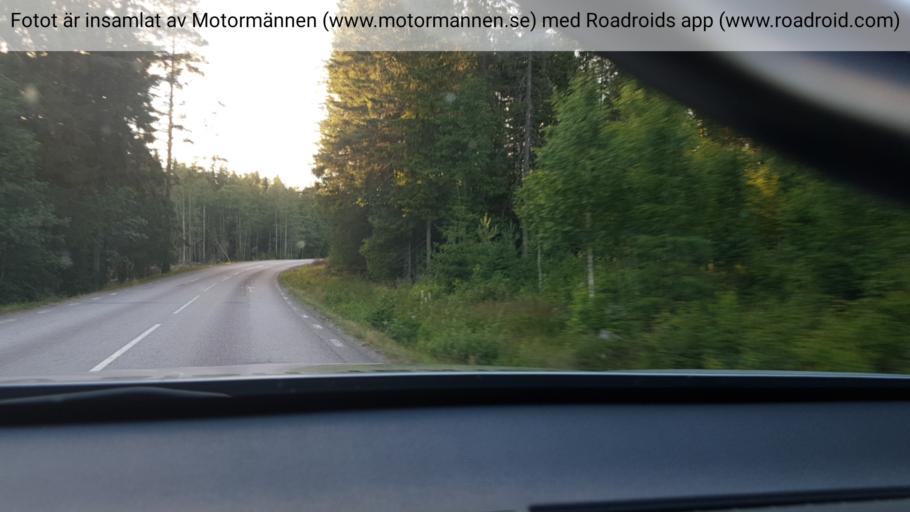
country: SE
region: Vaermland
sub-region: Torsby Kommun
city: Torsby
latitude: 60.1003
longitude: 13.0728
